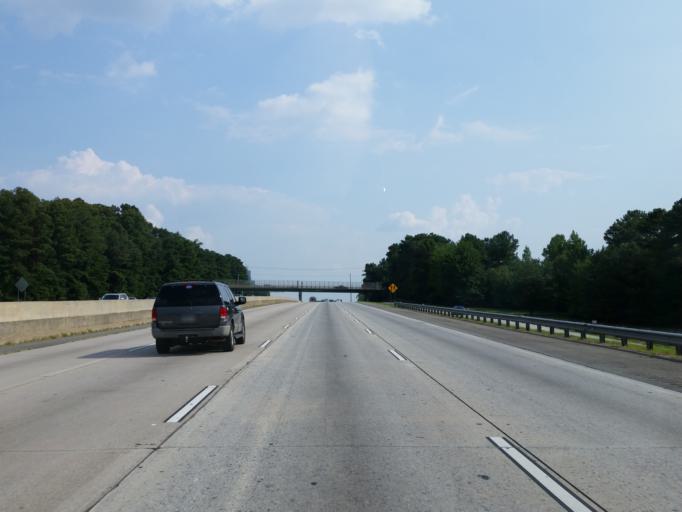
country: US
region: Georgia
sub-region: Fulton County
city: Sandy Springs
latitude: 33.9326
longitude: -84.3580
